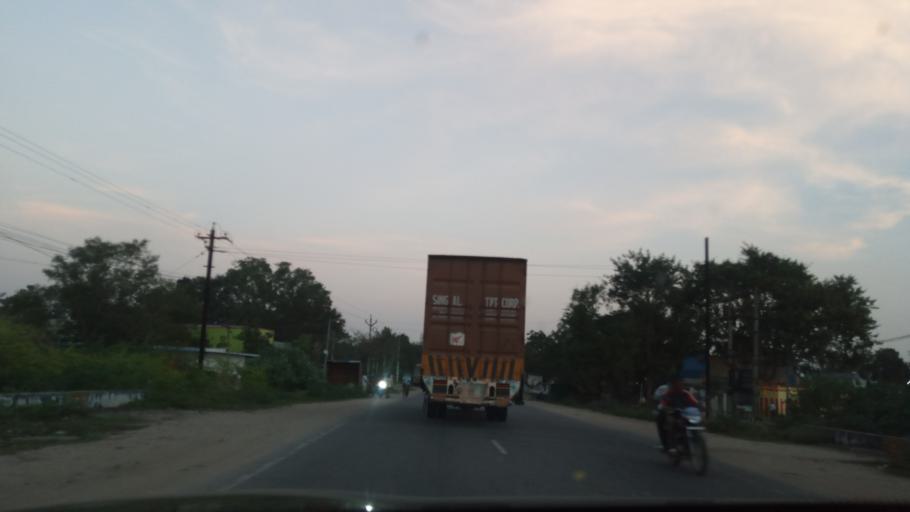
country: IN
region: Tamil Nadu
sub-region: Vellore
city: Walajapet
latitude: 12.9295
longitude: 79.3418
